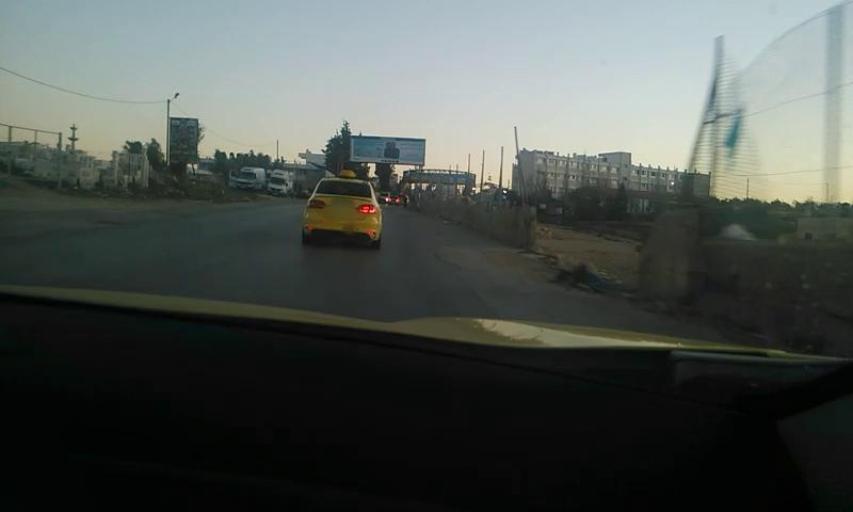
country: PS
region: West Bank
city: Jifna
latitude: 31.9466
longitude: 35.2159
